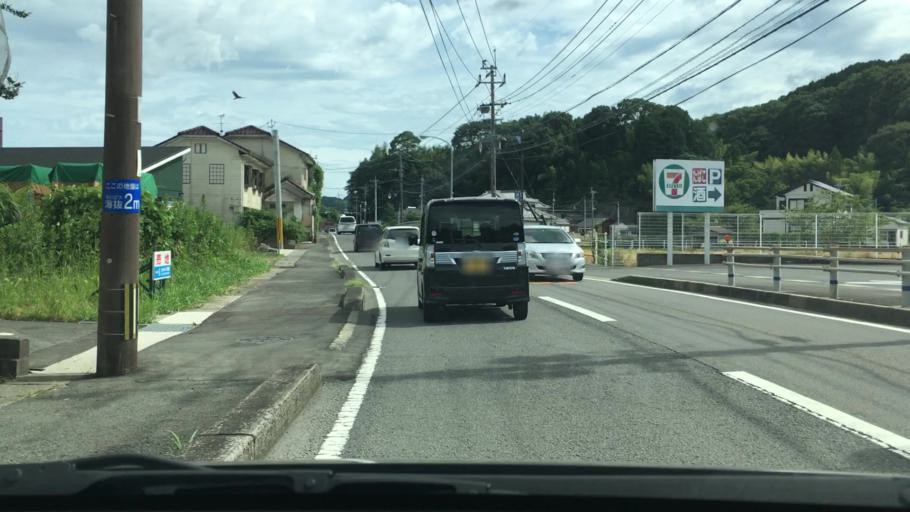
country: JP
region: Nagasaki
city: Togitsu
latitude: 32.9139
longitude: 129.7845
